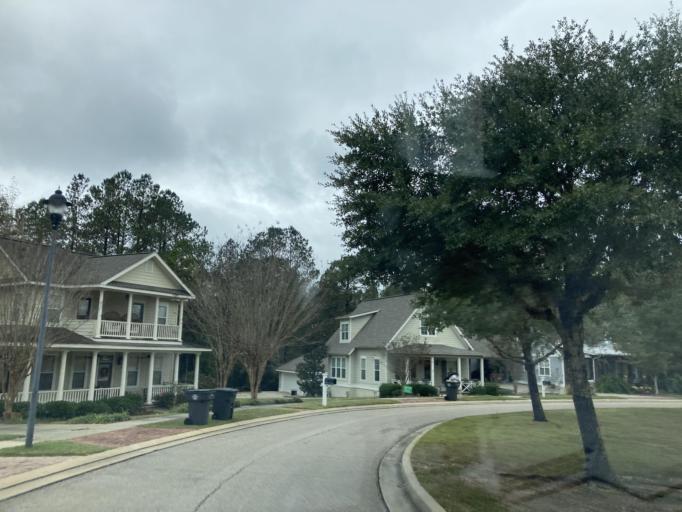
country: US
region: Mississippi
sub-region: Lamar County
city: West Hattiesburg
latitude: 31.2853
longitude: -89.4839
